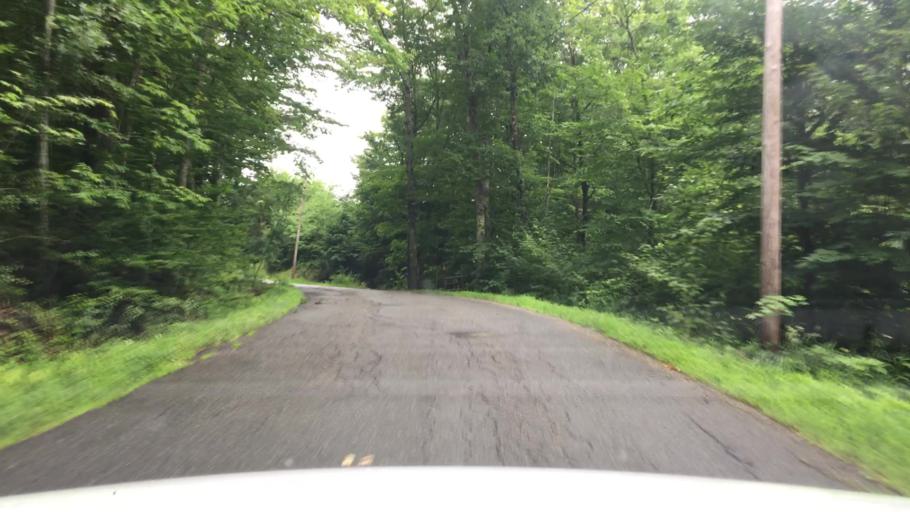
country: US
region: Maine
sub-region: Knox County
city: Hope
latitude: 44.2333
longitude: -69.1803
